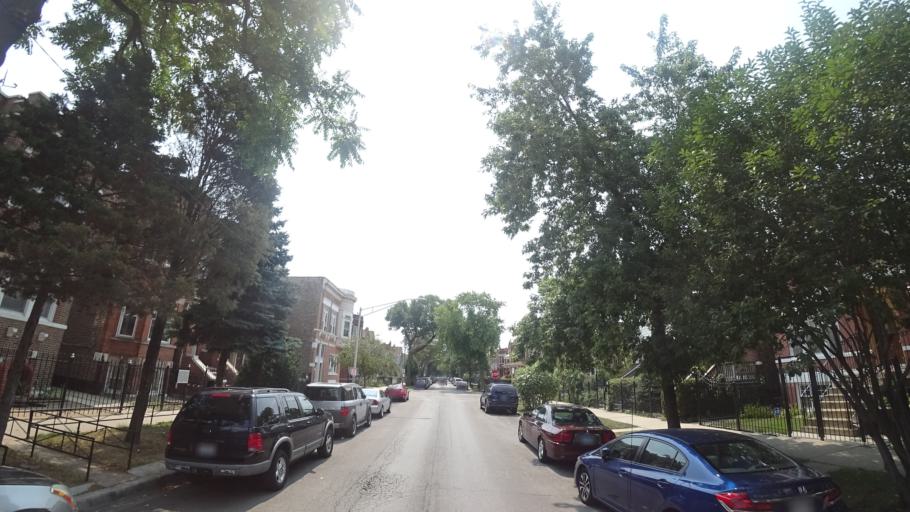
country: US
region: Illinois
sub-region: Cook County
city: Cicero
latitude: 41.8428
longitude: -87.7294
